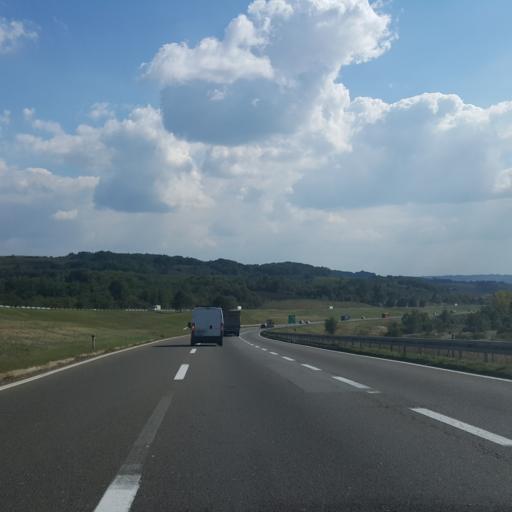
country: RS
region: Central Serbia
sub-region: Belgrade
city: Grocka
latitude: 44.6162
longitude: 20.6401
